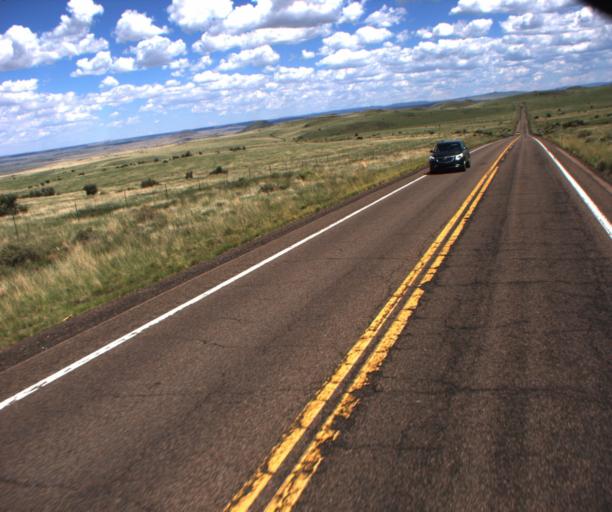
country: US
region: Arizona
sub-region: Apache County
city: Springerville
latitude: 34.2174
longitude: -109.4683
